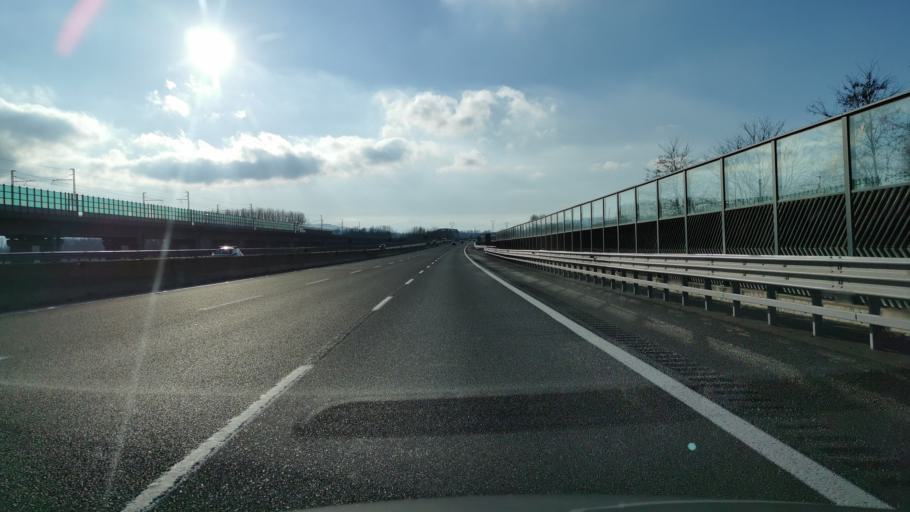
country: IT
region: Piedmont
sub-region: Provincia di Vercelli
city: Saluggia
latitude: 45.2509
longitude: 7.9930
